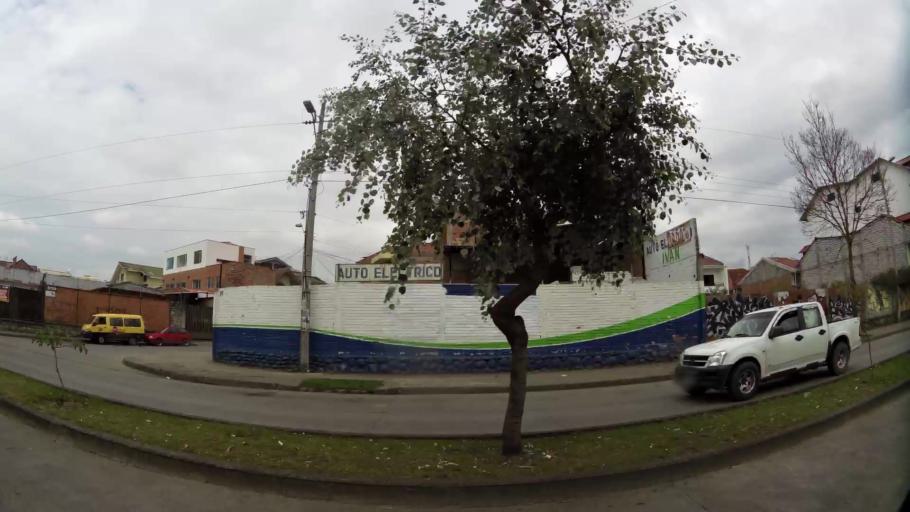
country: EC
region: Azuay
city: Cuenca
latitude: -2.9022
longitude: -78.9803
